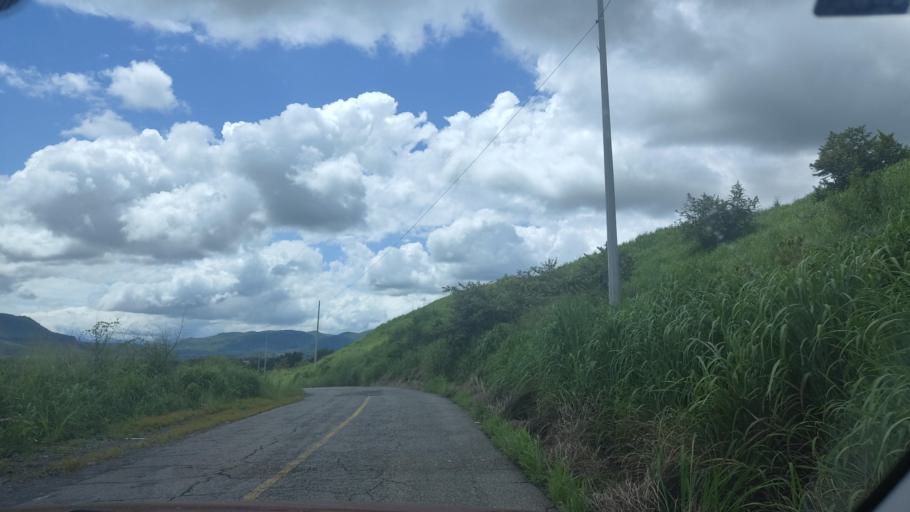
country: MX
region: Nayarit
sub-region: Ahuacatlan
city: Ahuacatlan
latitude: 21.1287
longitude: -104.6046
